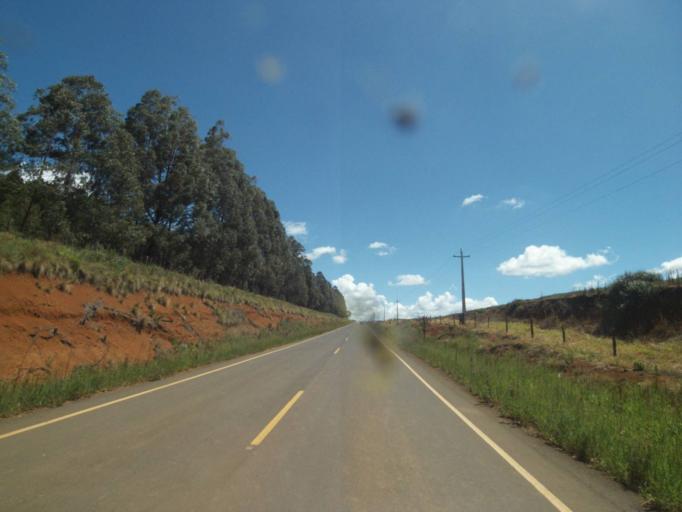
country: BR
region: Parana
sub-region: Pinhao
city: Pinhao
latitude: -25.8300
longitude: -52.0194
